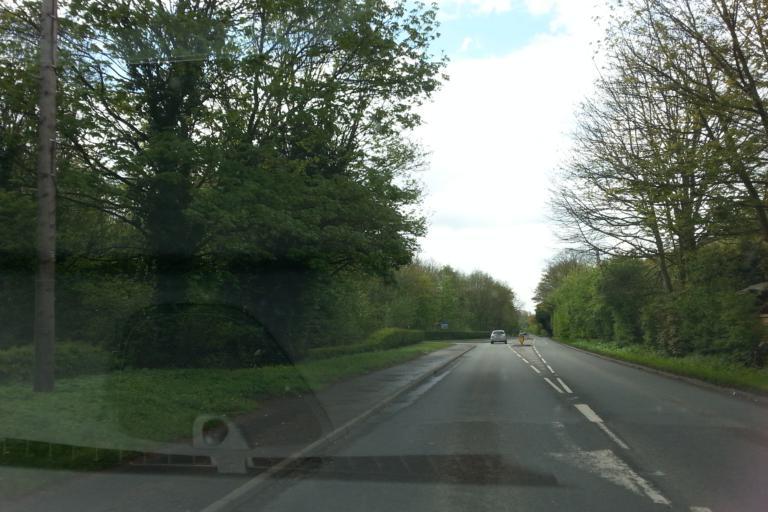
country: GB
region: England
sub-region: Staffordshire
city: Essington
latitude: 52.6352
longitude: -2.0443
